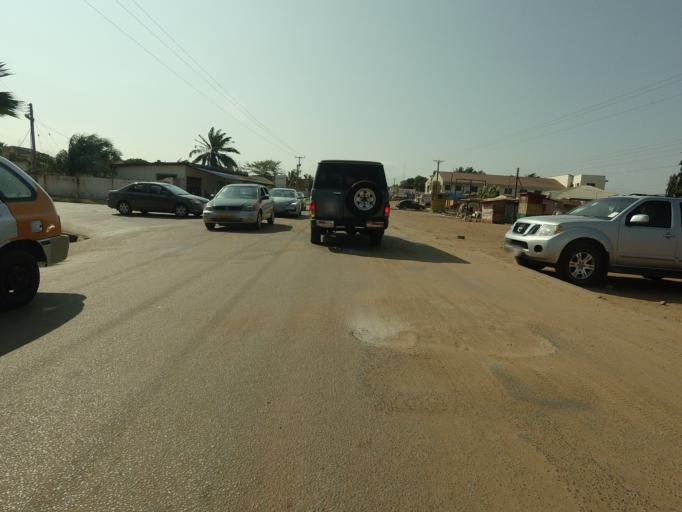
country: GH
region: Greater Accra
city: Teshi Old Town
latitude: 5.6014
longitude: -0.1038
